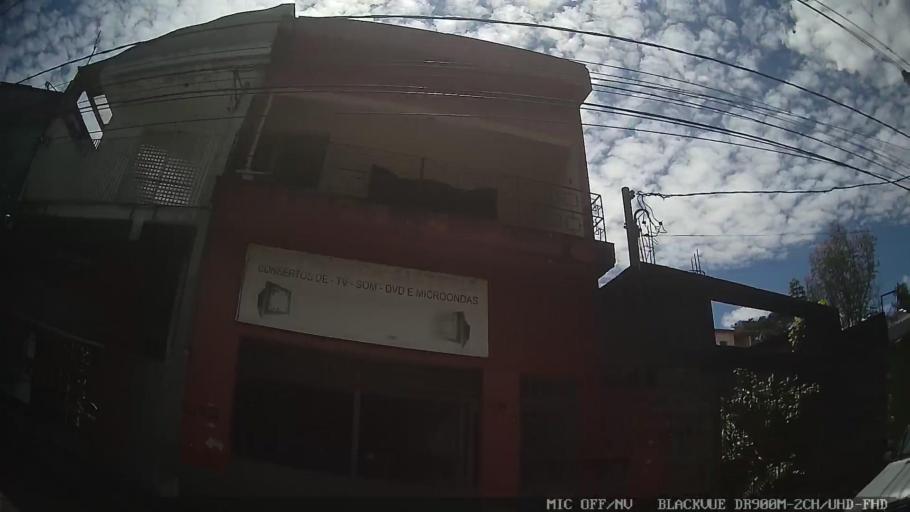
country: BR
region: Sao Paulo
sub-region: Biritiba-Mirim
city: Biritiba Mirim
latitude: -23.5763
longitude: -46.0385
